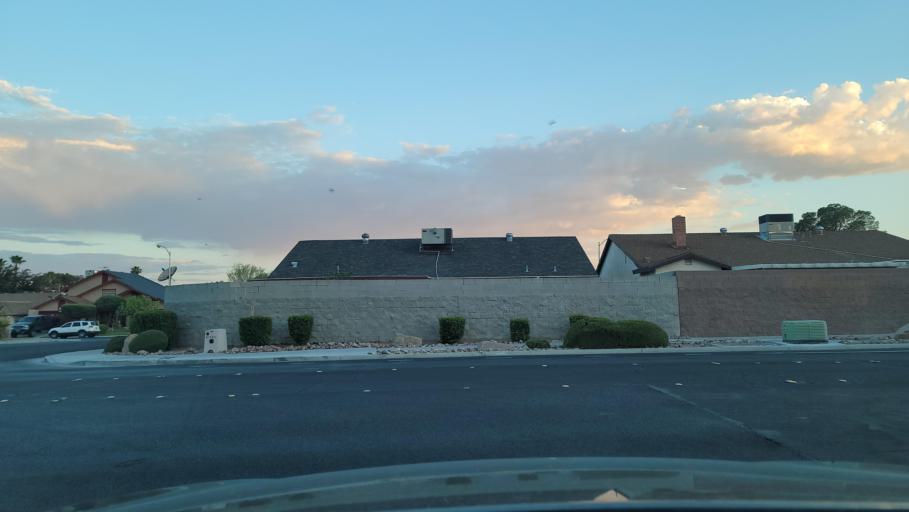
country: US
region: Nevada
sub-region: Clark County
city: Spring Valley
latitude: 36.1108
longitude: -115.2419
